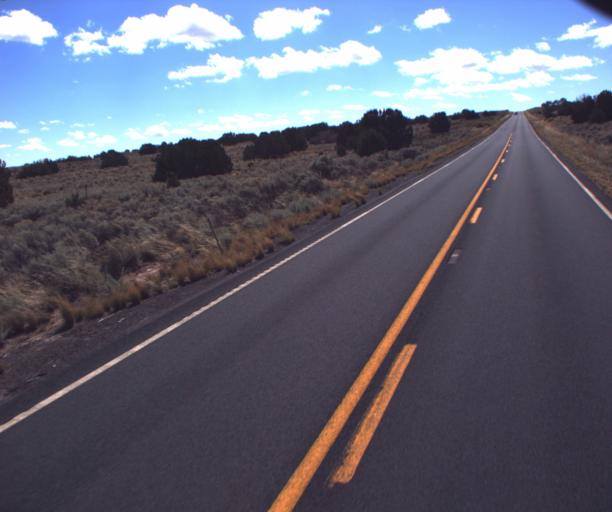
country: US
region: Arizona
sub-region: Apache County
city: Houck
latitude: 35.1600
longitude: -109.3365
